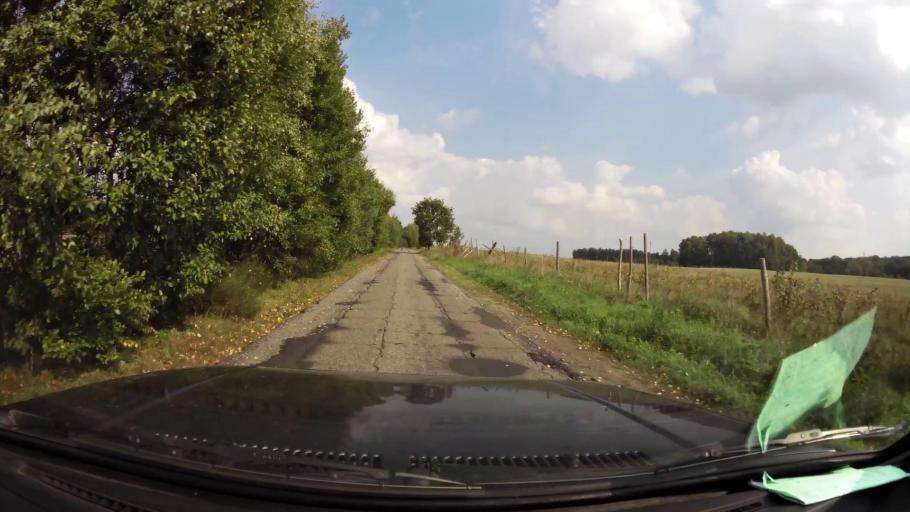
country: PL
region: West Pomeranian Voivodeship
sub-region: Powiat koszalinski
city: Polanow
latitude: 54.1180
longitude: 16.5107
